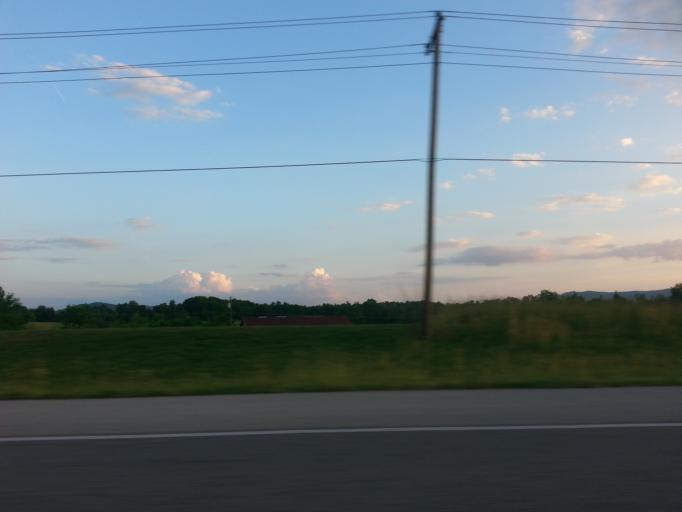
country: US
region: Tennessee
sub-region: Monroe County
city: Madisonville
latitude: 35.3934
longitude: -84.3424
